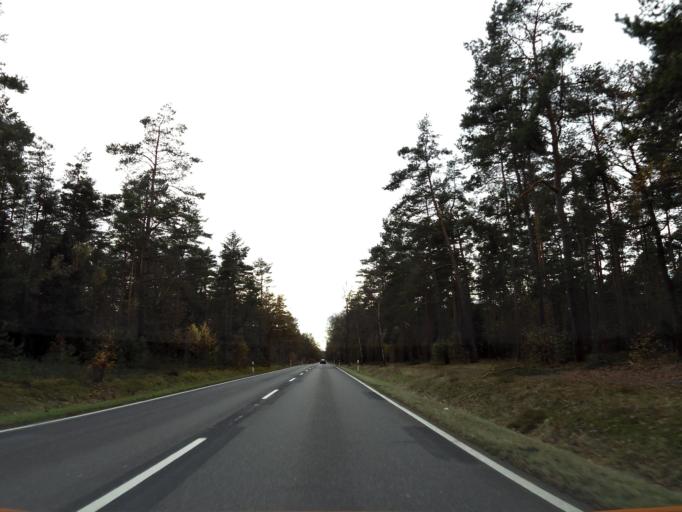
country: DE
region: Lower Saxony
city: Fassberg
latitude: 52.9767
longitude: 10.2152
